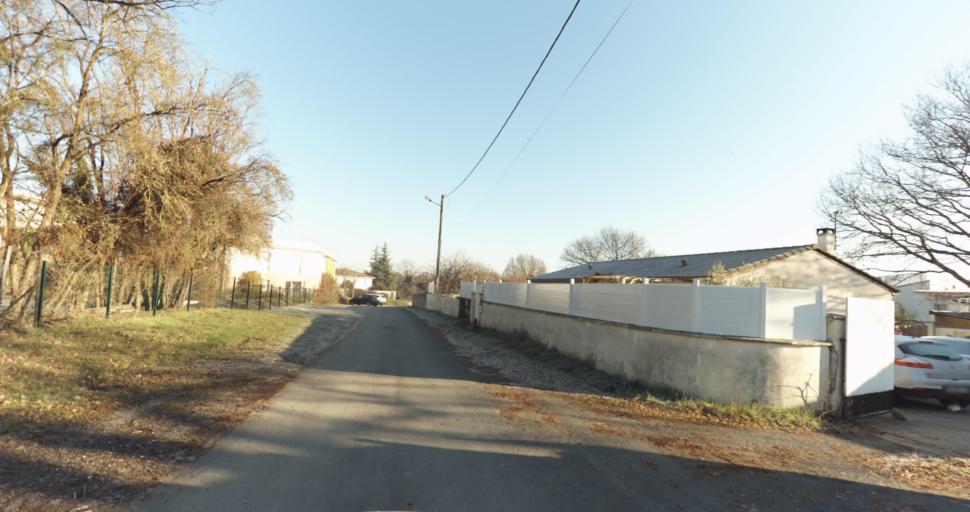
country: FR
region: Aquitaine
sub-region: Departement de la Gironde
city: Carbon-Blanc
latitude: 44.8998
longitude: -0.4997
